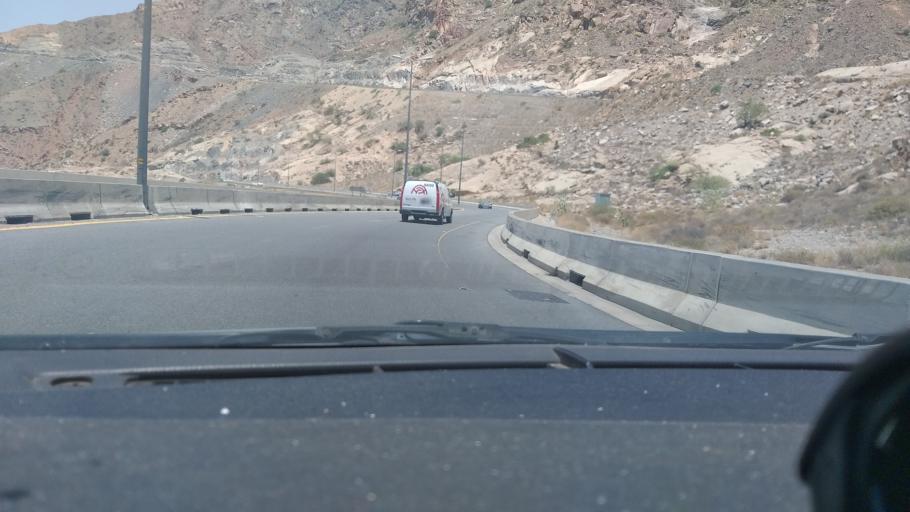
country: SA
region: Makkah
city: Al Hada
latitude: 21.3377
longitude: 40.2566
